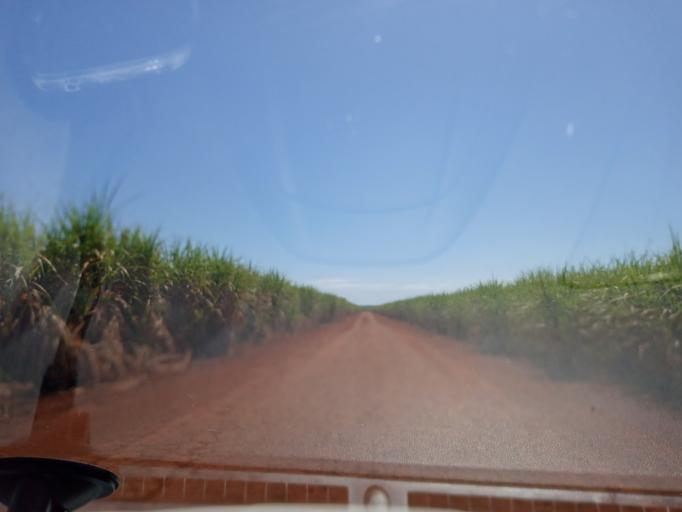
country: BR
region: Goias
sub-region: Itumbiara
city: Itumbiara
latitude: -18.4449
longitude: -49.1521
